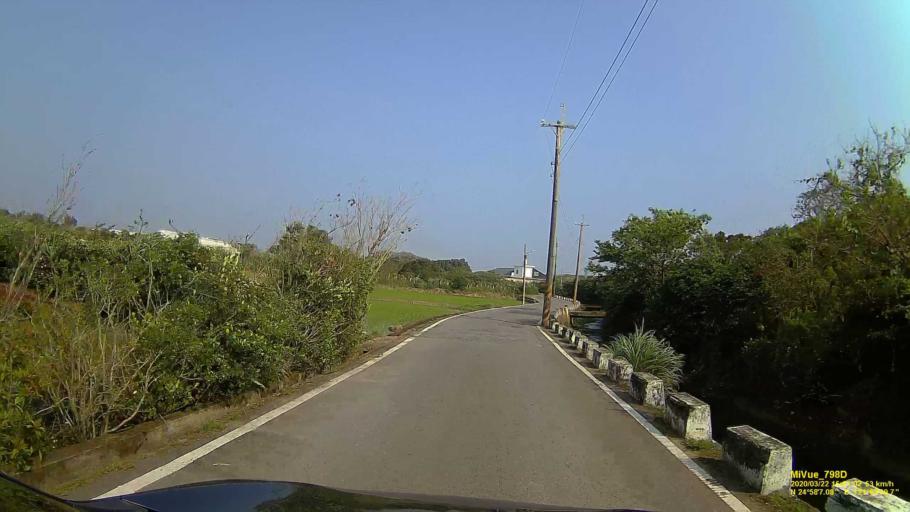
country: TW
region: Taiwan
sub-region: Hsinchu
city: Zhubei
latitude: 24.9685
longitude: 121.0614
